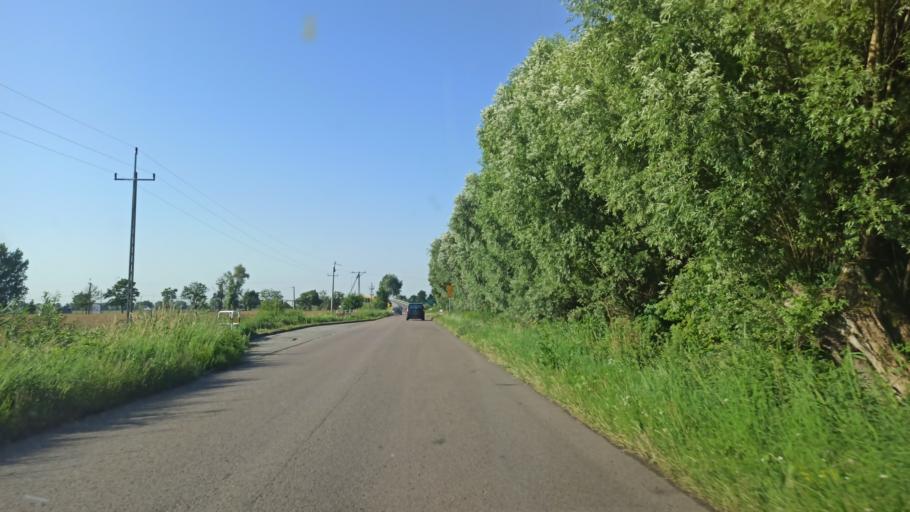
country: PL
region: Warmian-Masurian Voivodeship
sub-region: Powiat elblaski
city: Elblag
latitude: 54.1688
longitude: 19.3305
